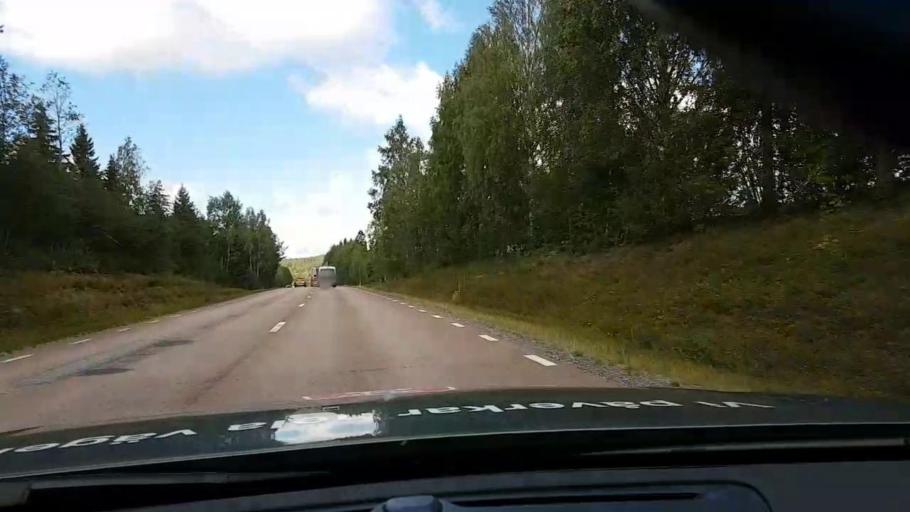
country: SE
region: Vaesternorrland
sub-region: OErnskoeldsviks Kommun
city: Bjasta
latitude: 63.3738
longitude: 18.4329
